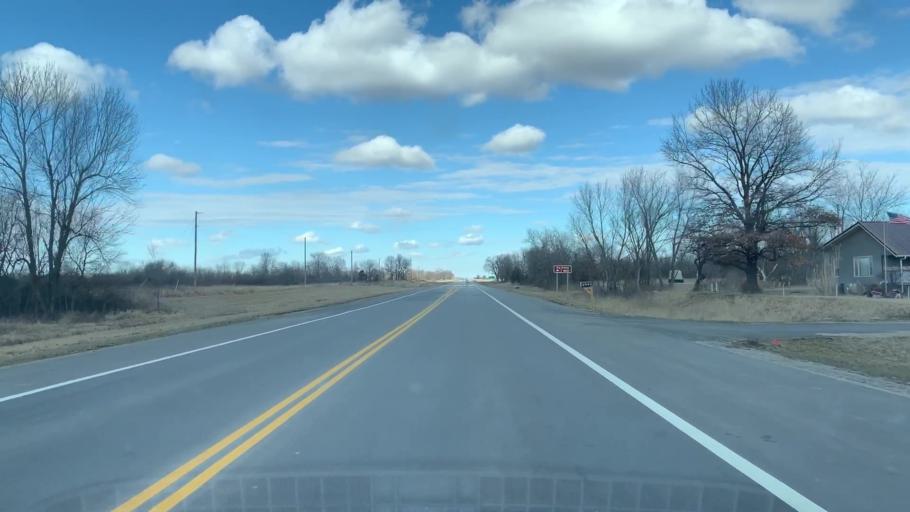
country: US
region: Kansas
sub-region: Cherokee County
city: Columbus
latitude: 37.2763
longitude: -94.8321
